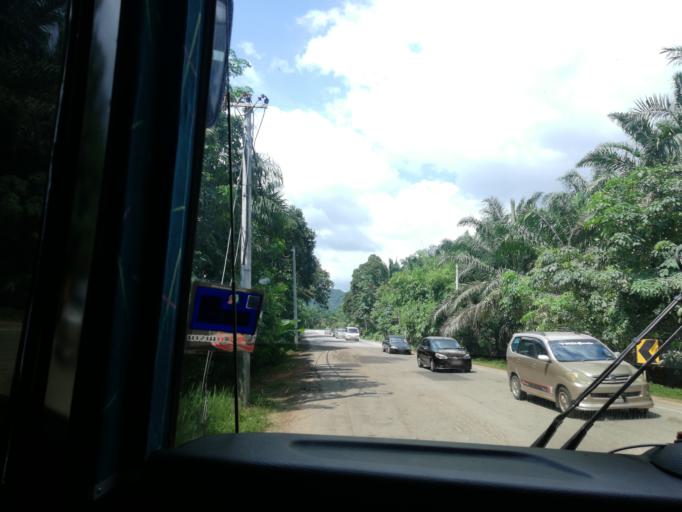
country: MY
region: Perak
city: Parit Buntar
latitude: 5.1213
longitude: 100.5665
